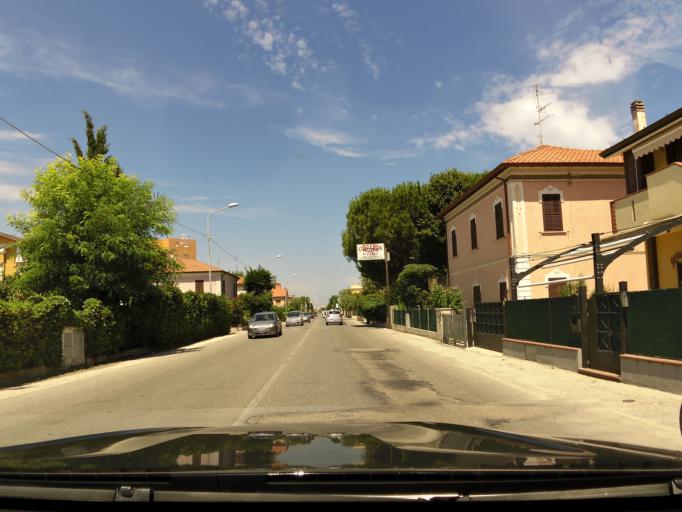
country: IT
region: The Marches
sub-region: Provincia di Ancona
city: Senigallia
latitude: 43.7328
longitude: 13.1943
